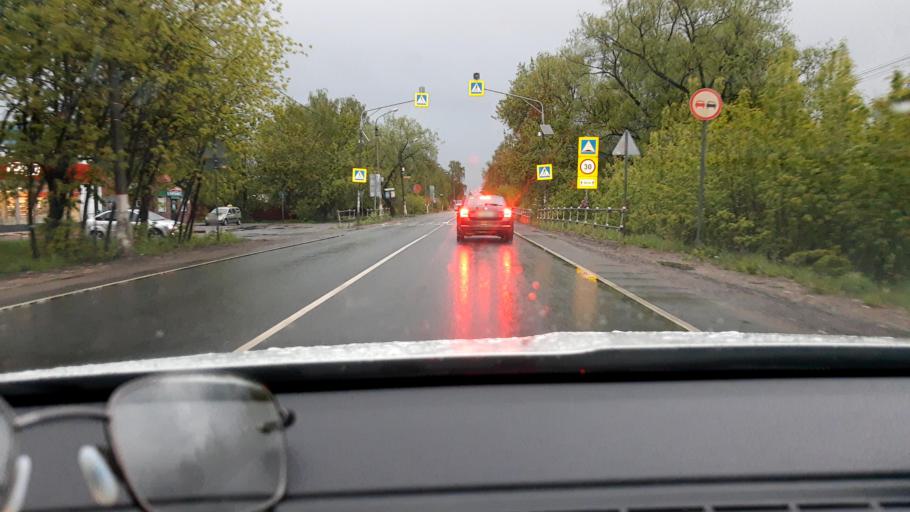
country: RU
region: Moskovskaya
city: Ivanteyevka
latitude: 55.9266
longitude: 37.9128
